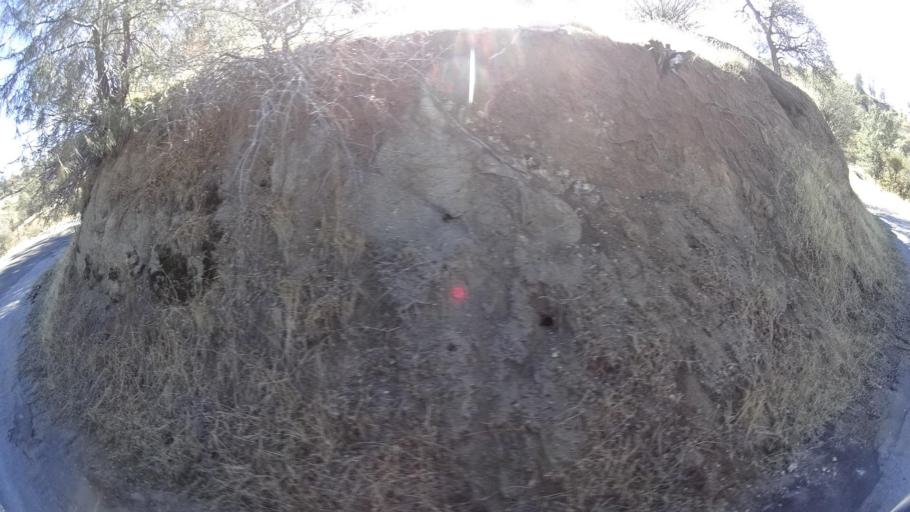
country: US
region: California
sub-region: Kern County
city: Bodfish
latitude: 35.4392
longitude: -118.7033
